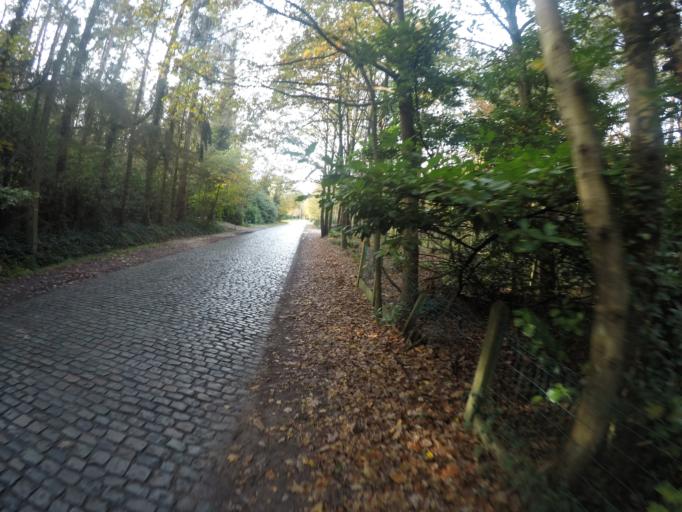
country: BE
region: Flanders
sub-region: Provincie Oost-Vlaanderen
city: Temse
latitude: 51.1689
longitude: 4.1967
